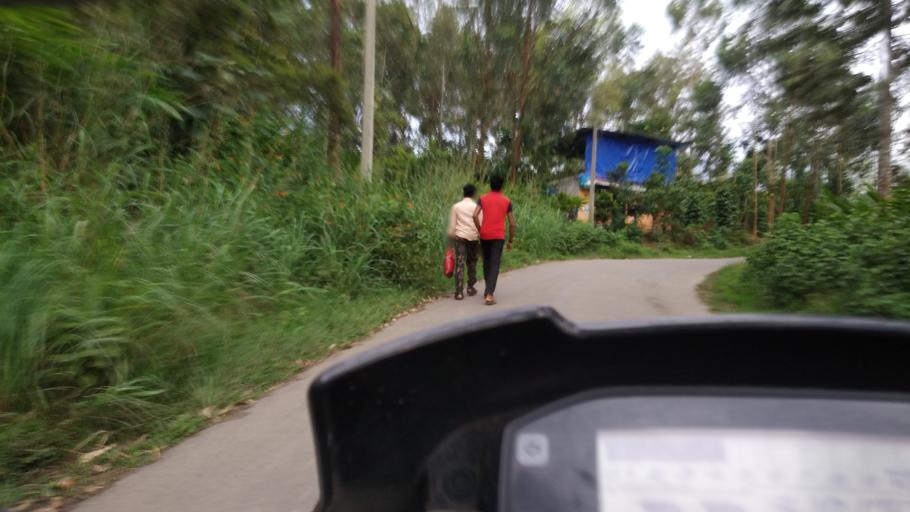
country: IN
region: Tamil Nadu
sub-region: Theni
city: Bodinayakkanur
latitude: 10.0256
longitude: 77.2319
